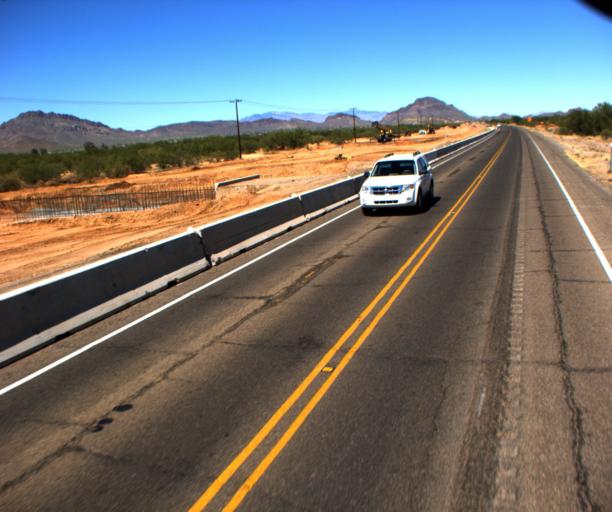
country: US
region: Arizona
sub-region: Pima County
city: Valencia West
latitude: 32.1435
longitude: -111.1414
